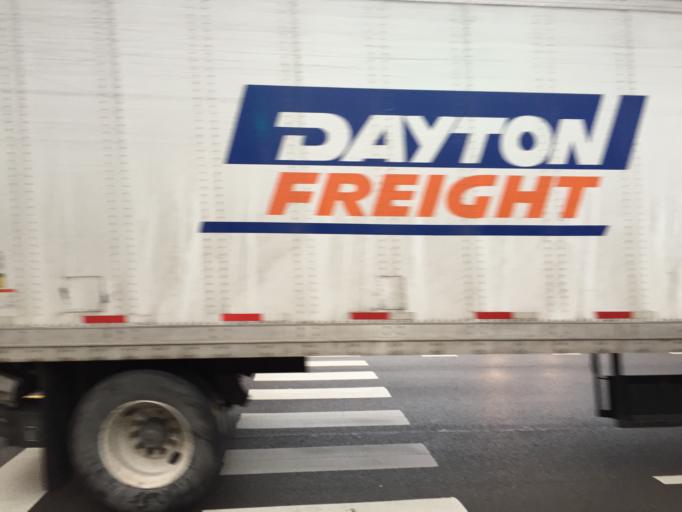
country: US
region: Illinois
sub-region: Cook County
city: Chicago
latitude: 41.8649
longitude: -87.6469
